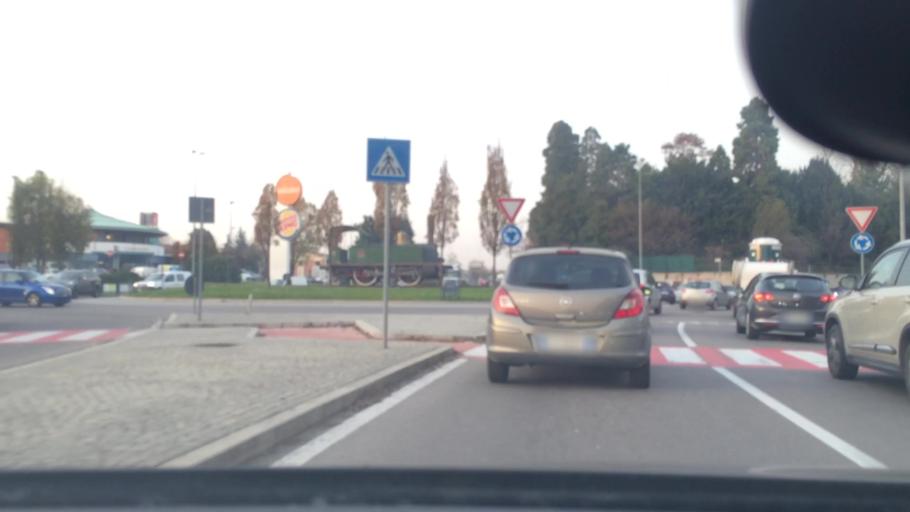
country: IT
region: Lombardy
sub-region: Provincia di Varese
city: Uboldo
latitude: 45.6220
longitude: 9.0188
